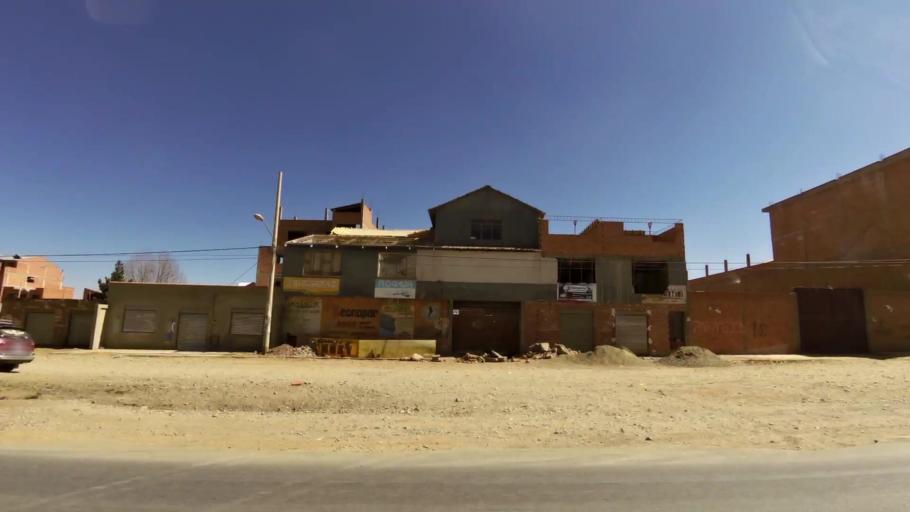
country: BO
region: La Paz
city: La Paz
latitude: -16.5447
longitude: -68.2001
